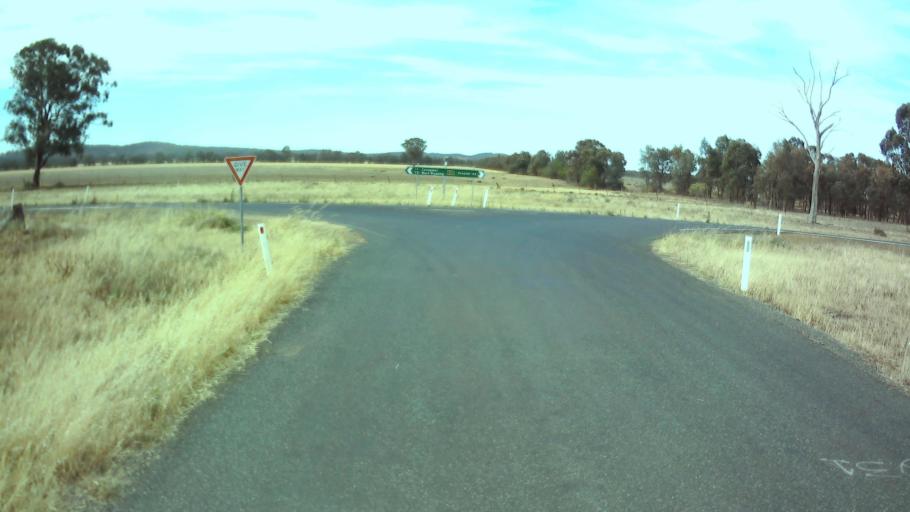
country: AU
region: New South Wales
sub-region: Weddin
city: Grenfell
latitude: -33.8565
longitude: 147.8607
